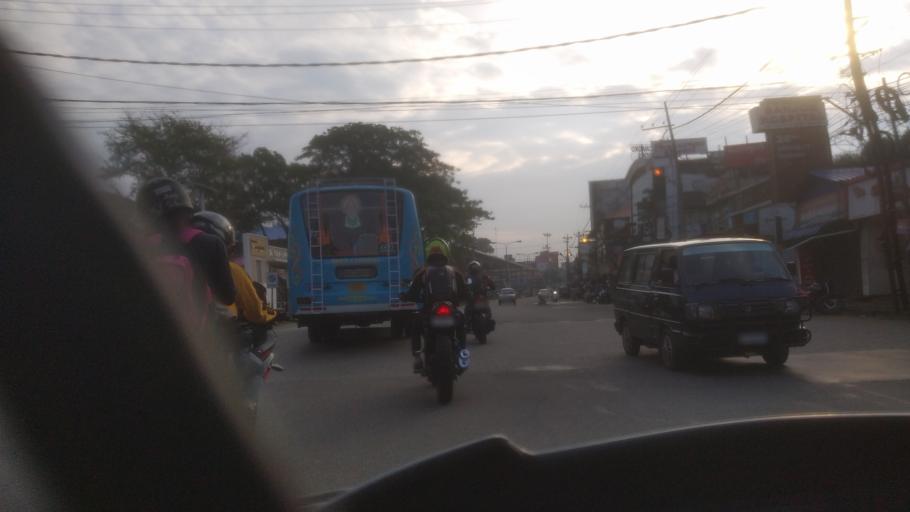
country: IN
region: Kerala
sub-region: Ernakulam
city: Perumpavur
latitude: 10.1151
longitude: 76.4726
